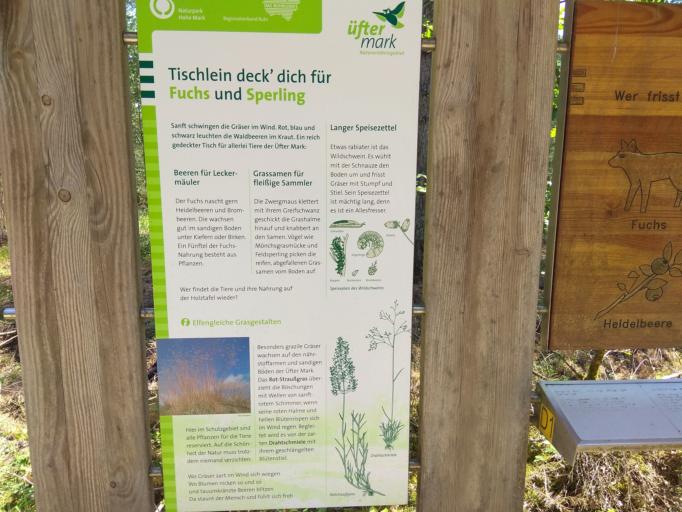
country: DE
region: North Rhine-Westphalia
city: Dorsten
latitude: 51.7221
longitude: 6.9438
